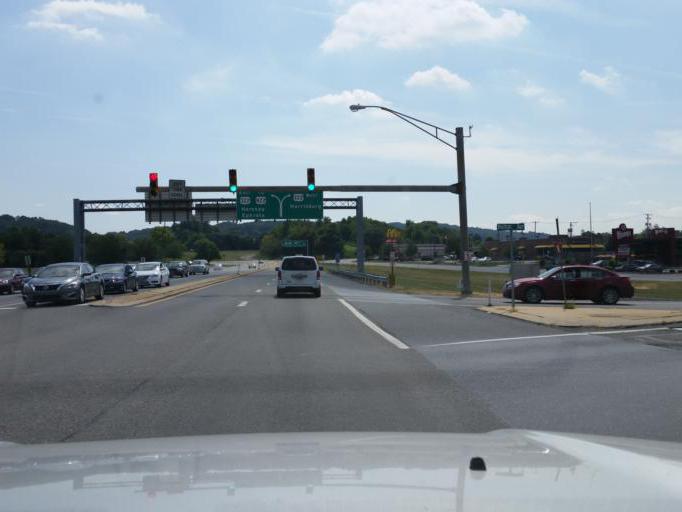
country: US
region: Pennsylvania
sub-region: Dauphin County
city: Hummelstown
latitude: 40.2698
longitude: -76.6892
